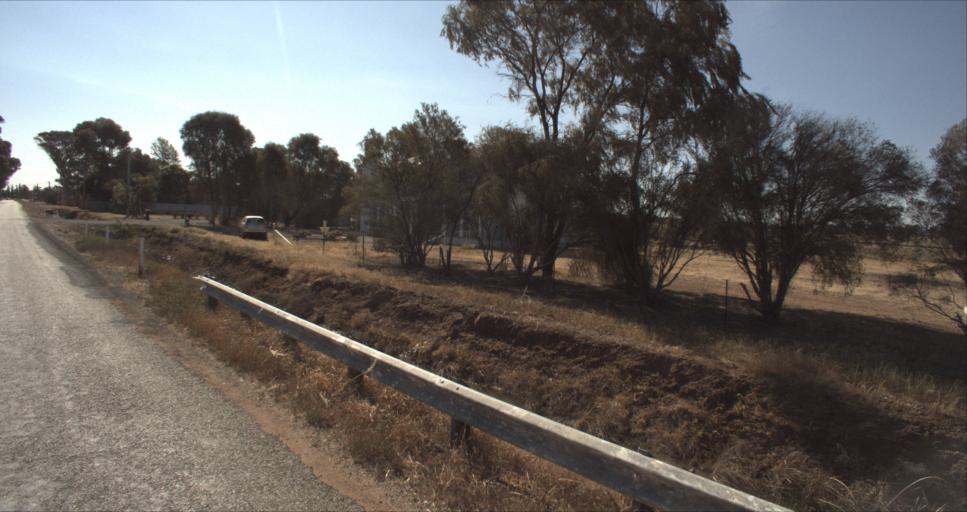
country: AU
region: New South Wales
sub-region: Leeton
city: Leeton
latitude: -34.5356
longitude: 146.4198
